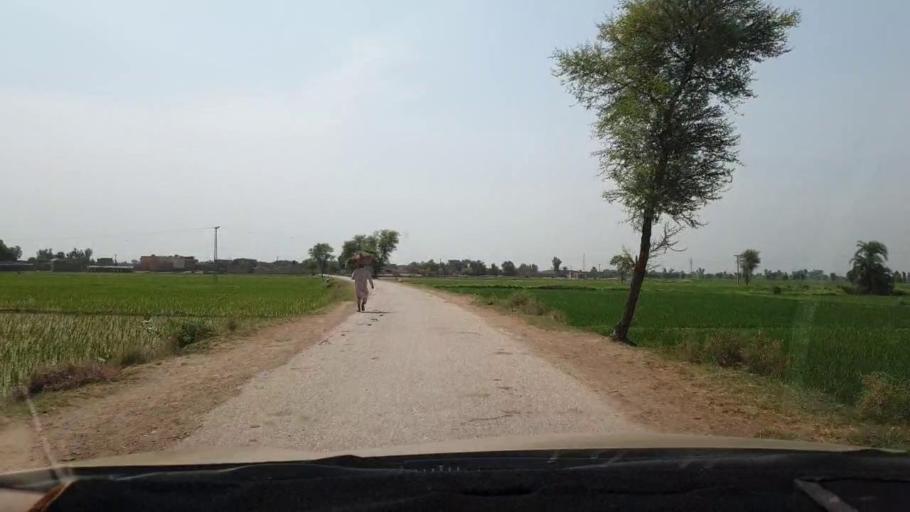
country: PK
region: Sindh
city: Naudero
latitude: 27.6360
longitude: 68.2735
